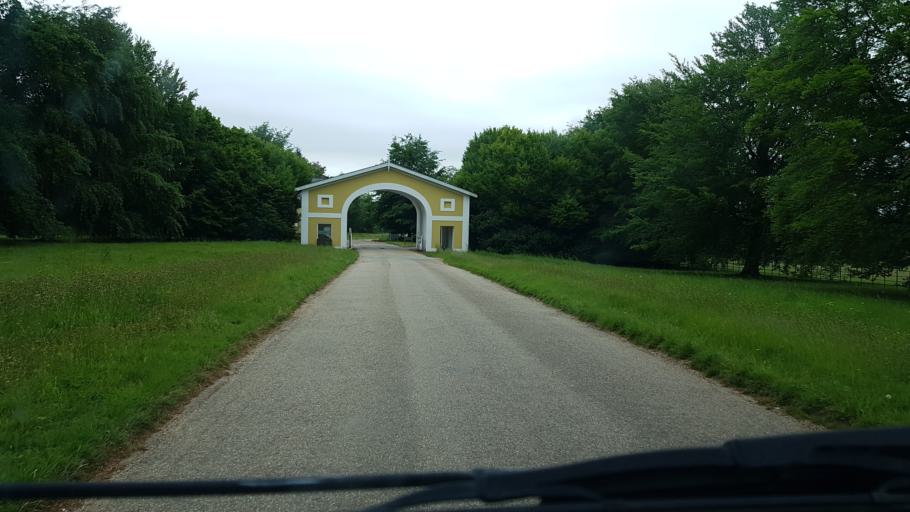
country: GB
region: England
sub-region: Surrey
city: Great Bookham
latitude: 51.2616
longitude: -0.3719
